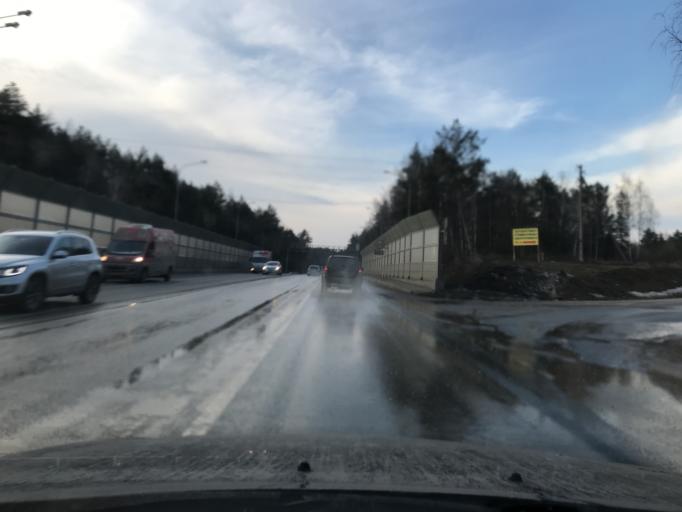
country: RU
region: Kaluga
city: Mstikhino
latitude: 54.5702
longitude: 36.1166
